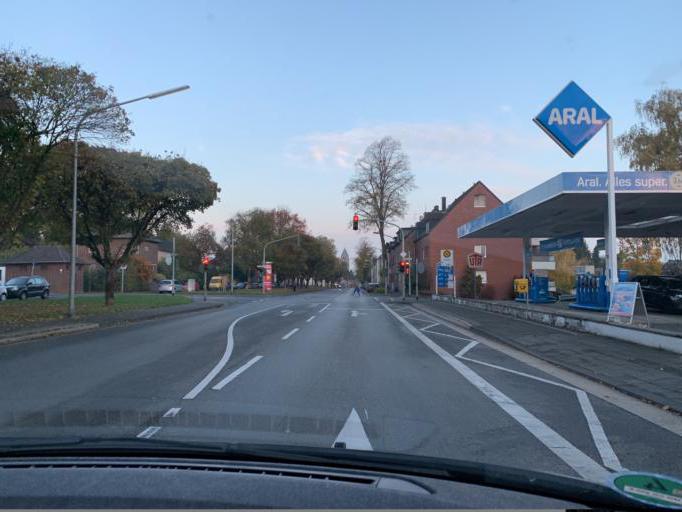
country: DE
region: North Rhine-Westphalia
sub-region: Regierungsbezirk Dusseldorf
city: Juchen
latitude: 51.1275
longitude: 6.4536
